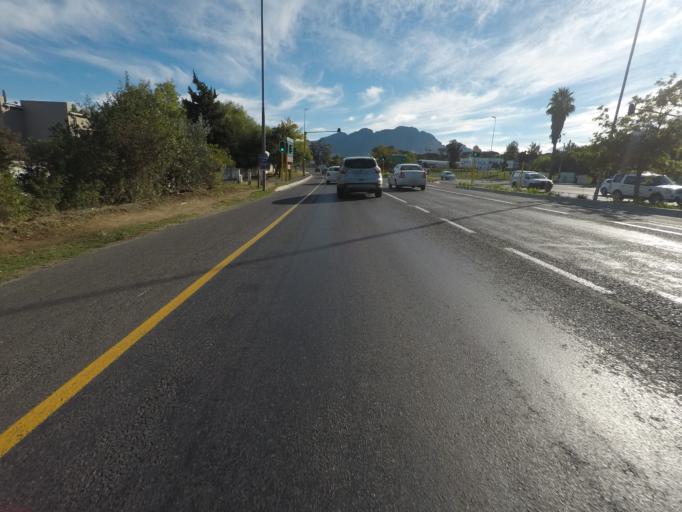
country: ZA
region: Western Cape
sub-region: Cape Winelands District Municipality
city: Stellenbosch
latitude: -33.9571
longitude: 18.8546
